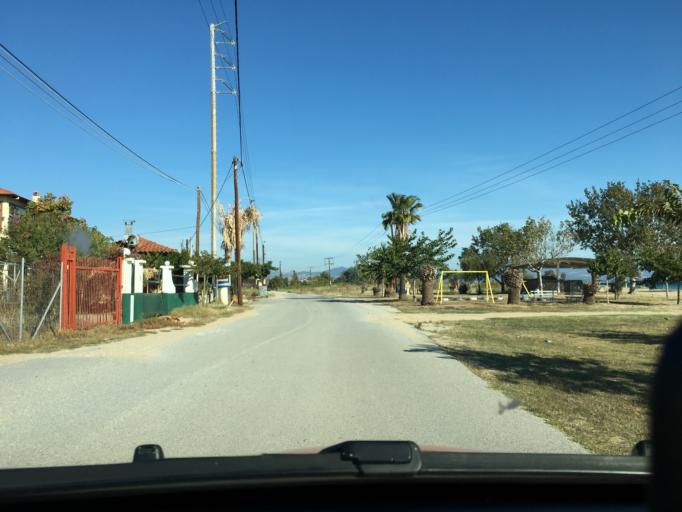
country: GR
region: Central Macedonia
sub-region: Nomos Chalkidikis
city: Nea Potidhaia
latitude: 40.2014
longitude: 23.3300
